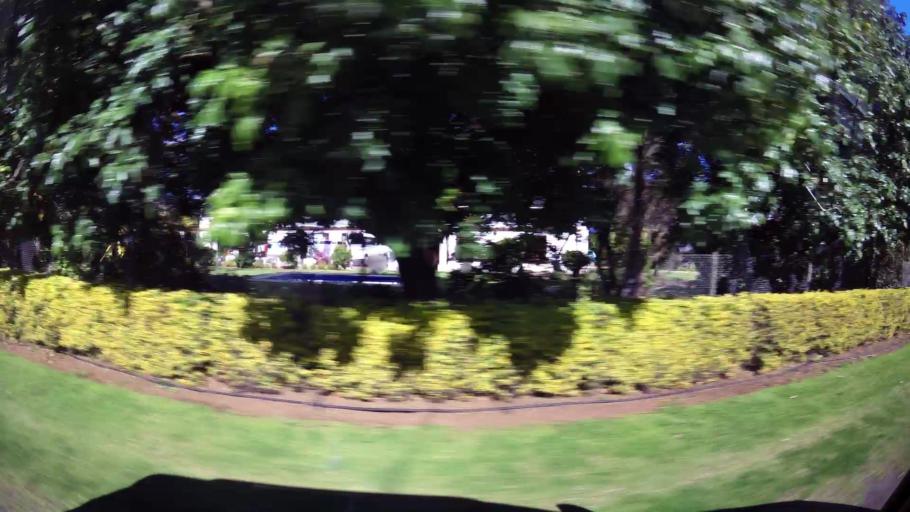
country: ZA
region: Western Cape
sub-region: Cape Winelands District Municipality
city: Ashton
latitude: -33.8062
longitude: 19.8644
